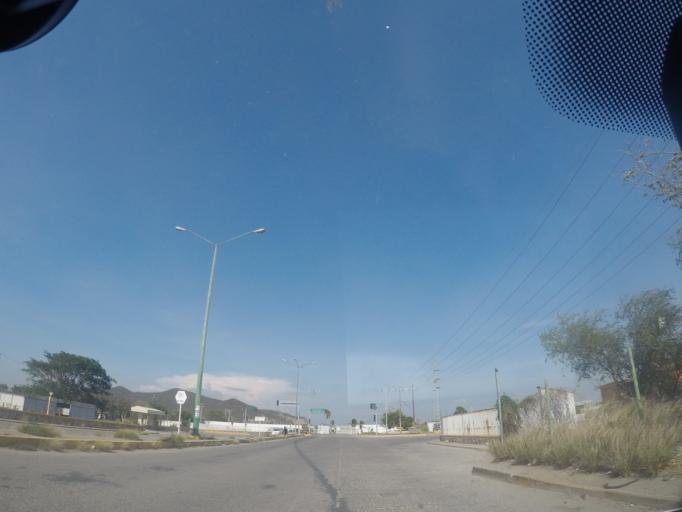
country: MX
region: Oaxaca
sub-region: Salina Cruz
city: Salina Cruz
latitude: 16.2197
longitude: -95.1910
